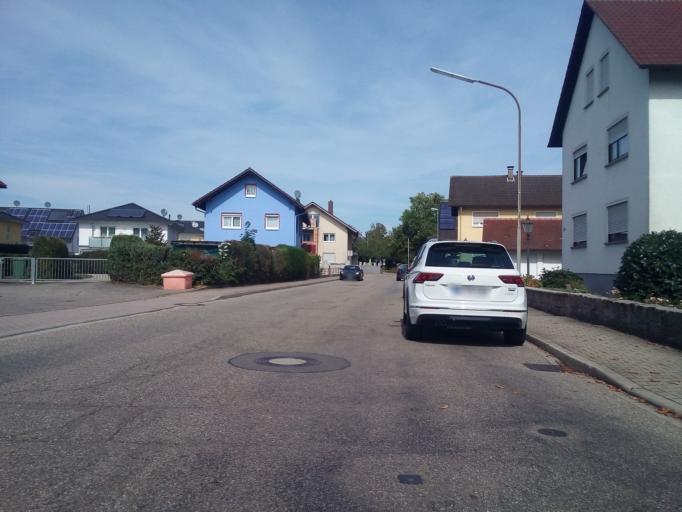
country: DE
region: Baden-Wuerttemberg
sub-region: Karlsruhe Region
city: Sinzheim
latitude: 48.7655
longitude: 8.1664
